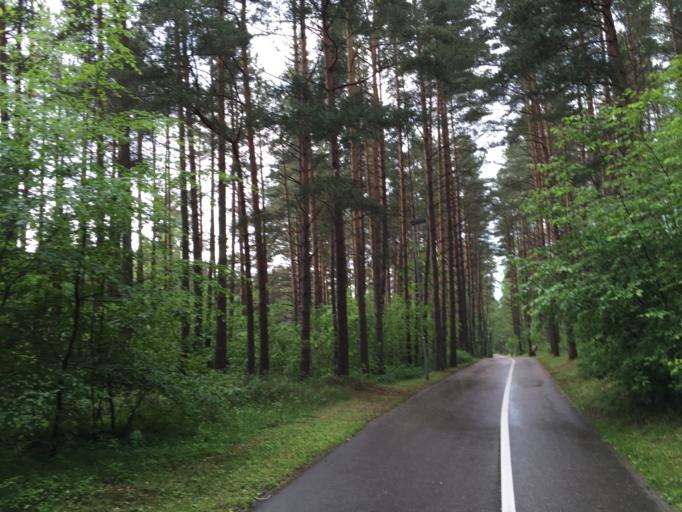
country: LT
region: Klaipedos apskritis
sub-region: Klaipeda
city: Klaipeda
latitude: 55.7492
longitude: 21.1188
